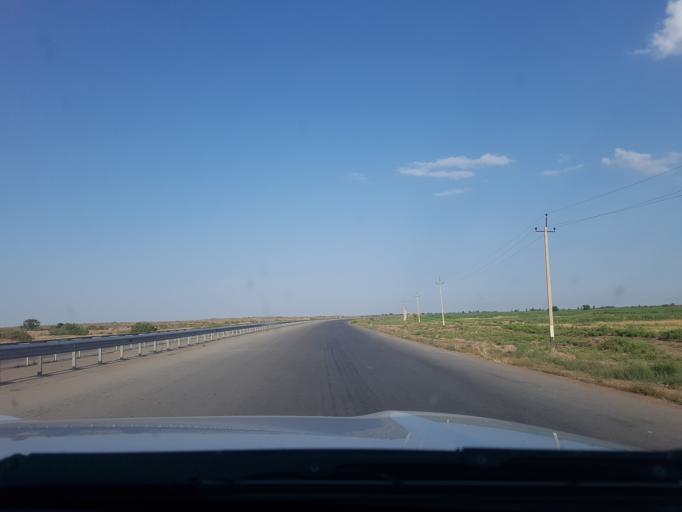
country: TM
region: Dasoguz
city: Yylanly
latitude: 41.7510
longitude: 59.3898
